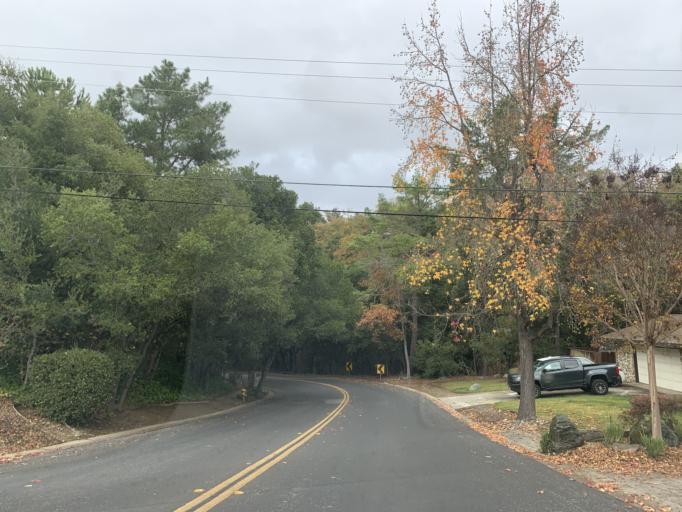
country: US
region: California
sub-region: Santa Clara County
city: Monte Sereno
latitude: 37.2574
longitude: -121.9916
